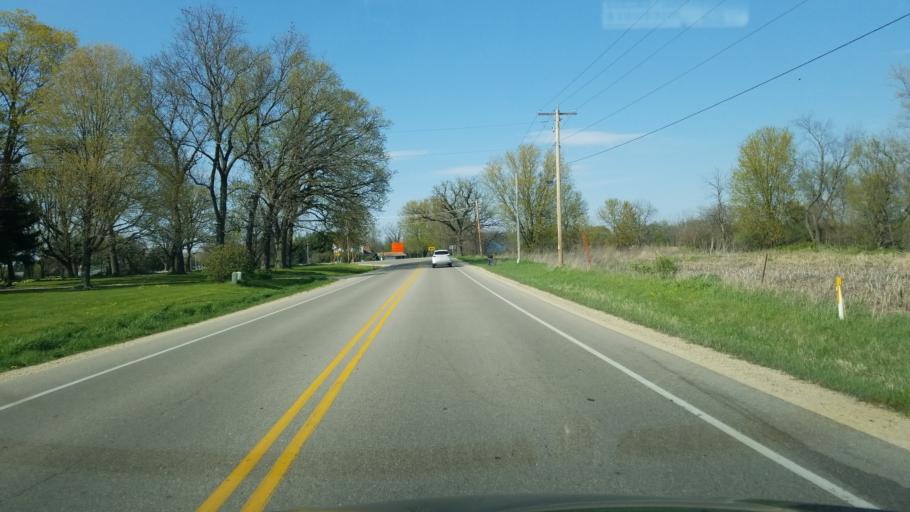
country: US
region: Wisconsin
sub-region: Dane County
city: Fitchburg
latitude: 42.9457
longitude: -89.4380
